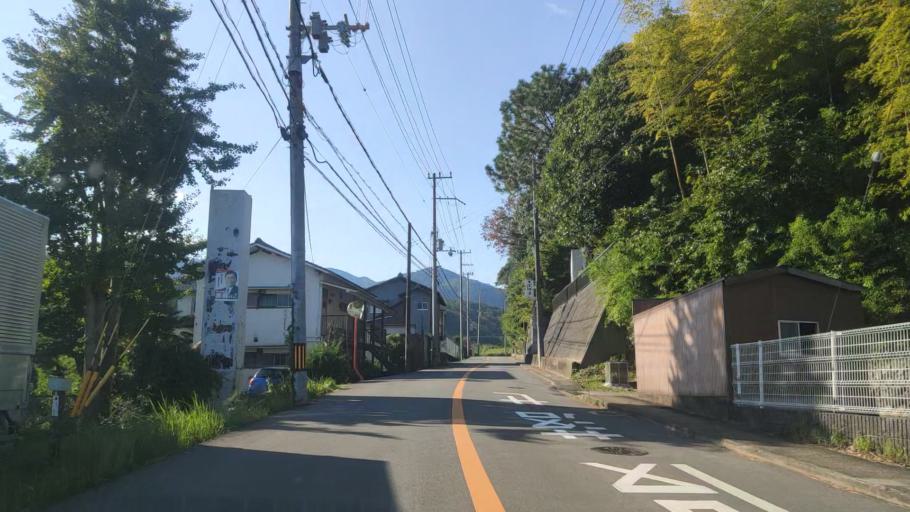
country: JP
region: Hyogo
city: Sandacho
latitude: 34.8105
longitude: 135.2504
